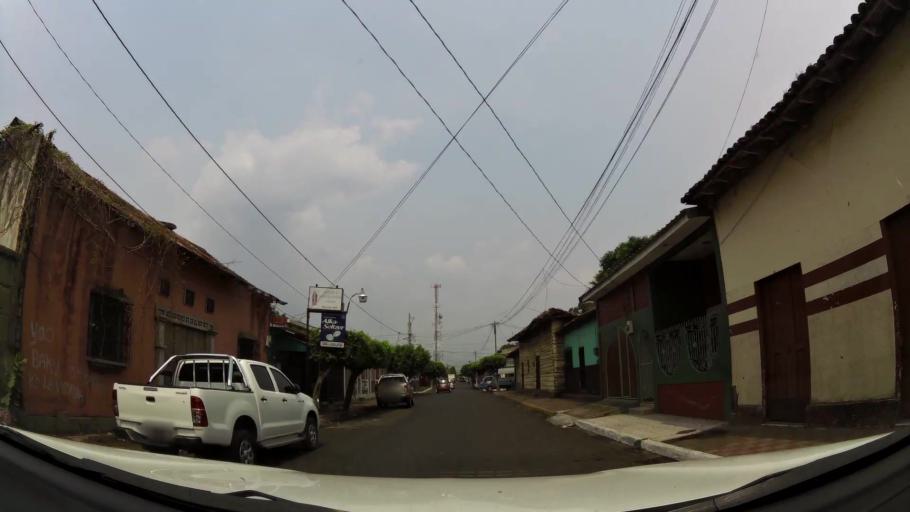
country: NI
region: Chinandega
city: Chinandega
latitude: 12.6267
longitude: -87.1308
